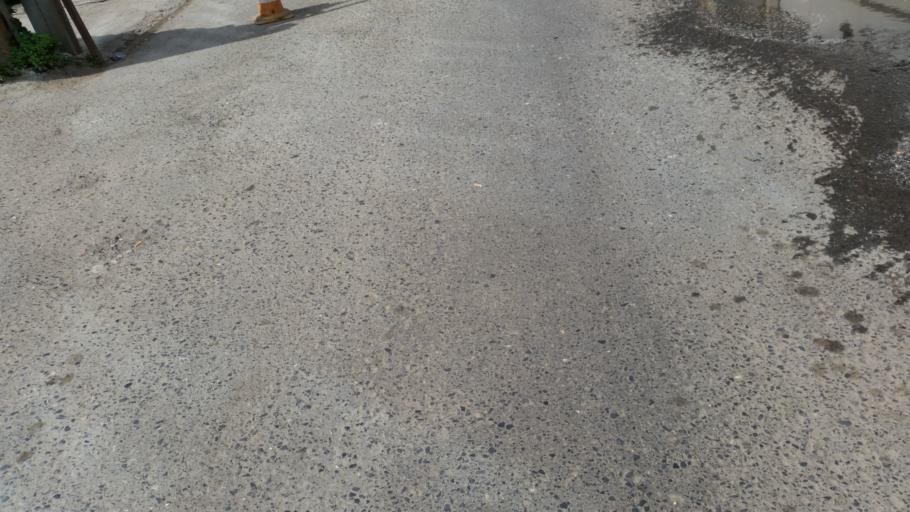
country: TR
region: Istanbul
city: Eminoenue
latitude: 41.0368
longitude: 28.9705
